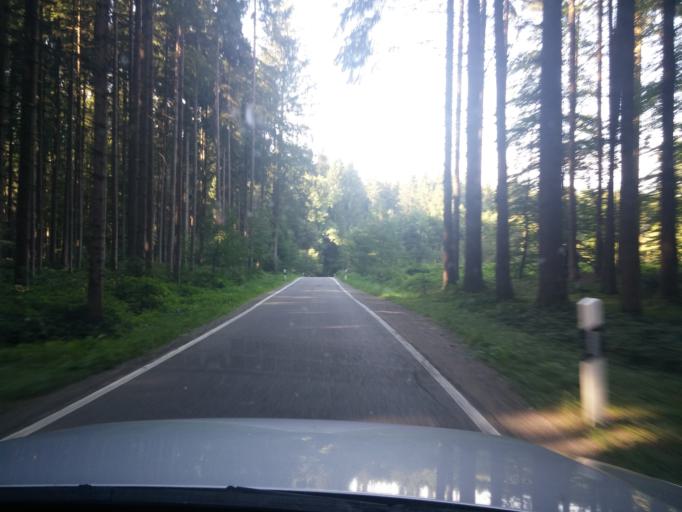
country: DE
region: Baden-Wuerttemberg
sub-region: Tuebingen Region
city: Aichstetten
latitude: 47.8512
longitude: 10.0872
